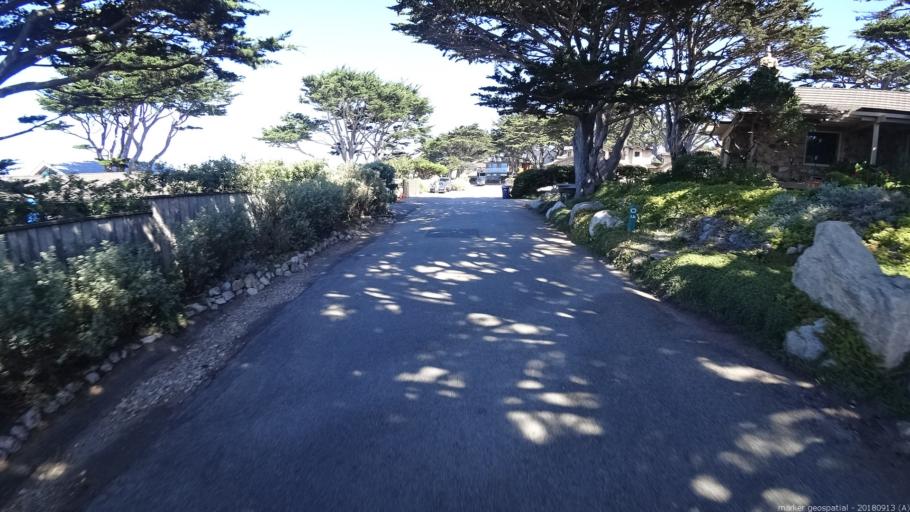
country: US
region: California
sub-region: Monterey County
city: Carmel-by-the-Sea
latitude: 36.5408
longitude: -121.9326
